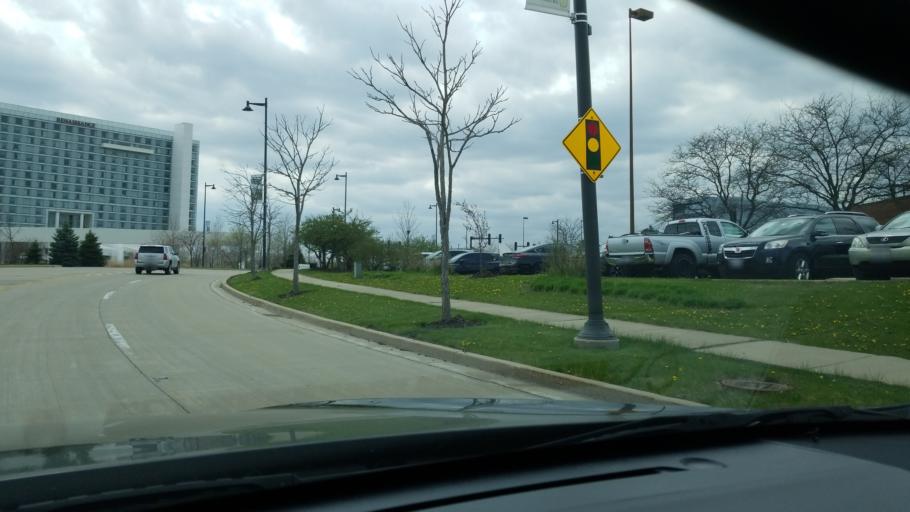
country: US
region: Illinois
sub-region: Cook County
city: Rolling Meadows
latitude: 42.0634
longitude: -88.0403
